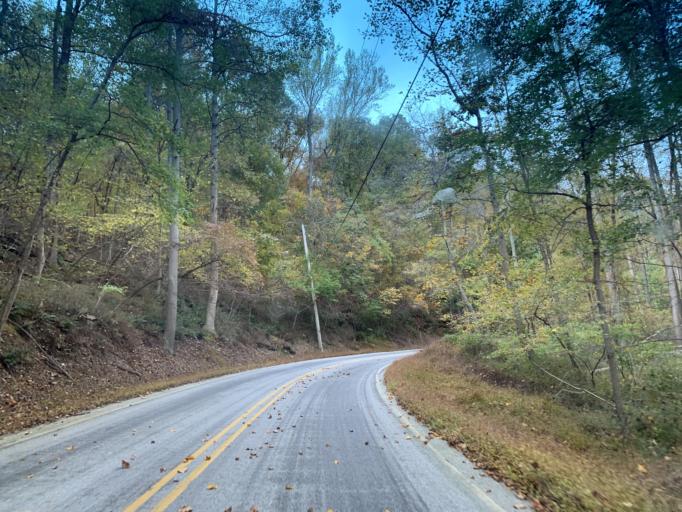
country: US
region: Pennsylvania
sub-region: York County
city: Stewartstown
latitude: 39.8307
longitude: -76.5135
